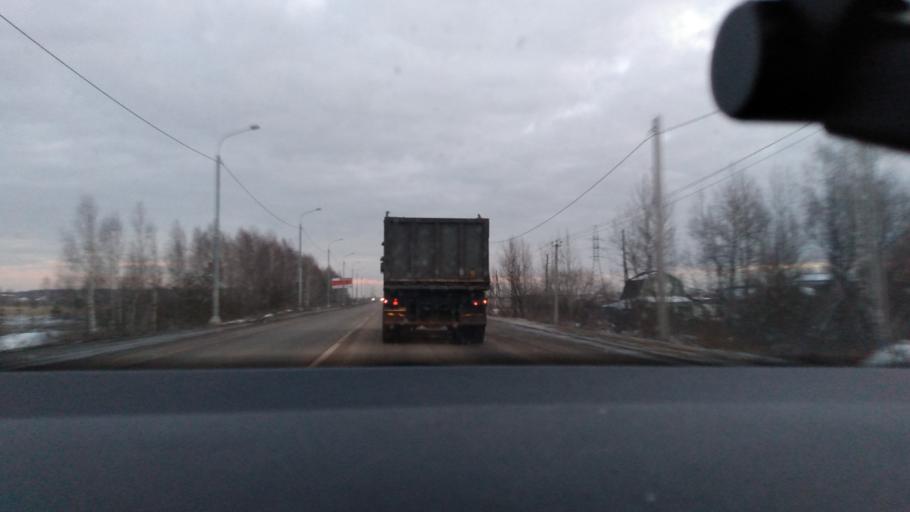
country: RU
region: Moskovskaya
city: Yegor'yevsk
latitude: 55.4083
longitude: 39.0527
